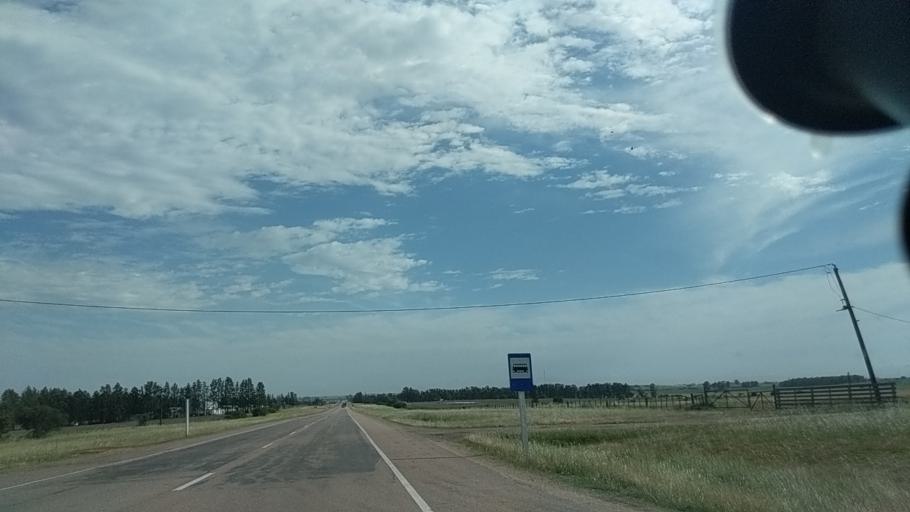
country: UY
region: Canelones
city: Canelones
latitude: -34.4143
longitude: -56.2605
